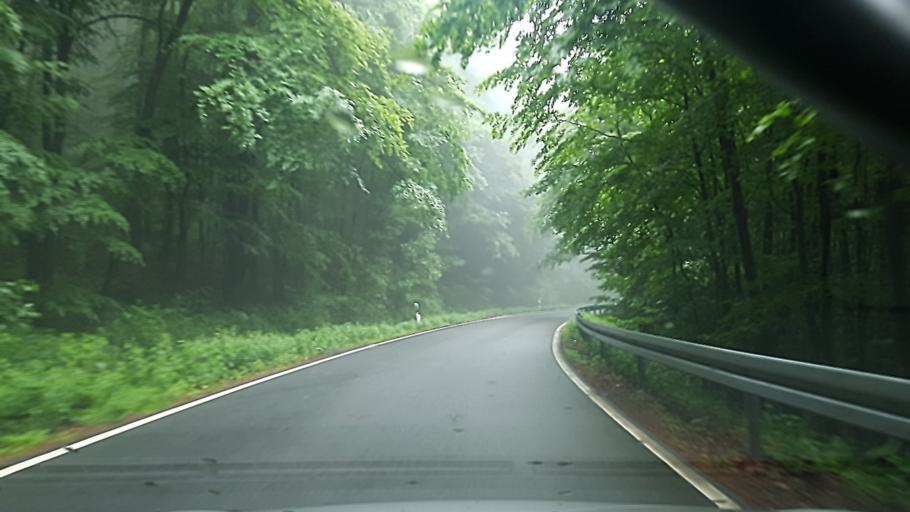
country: DE
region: Hesse
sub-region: Regierungsbezirk Darmstadt
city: Seeheim-Jugenheim
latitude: 49.7913
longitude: 8.6669
